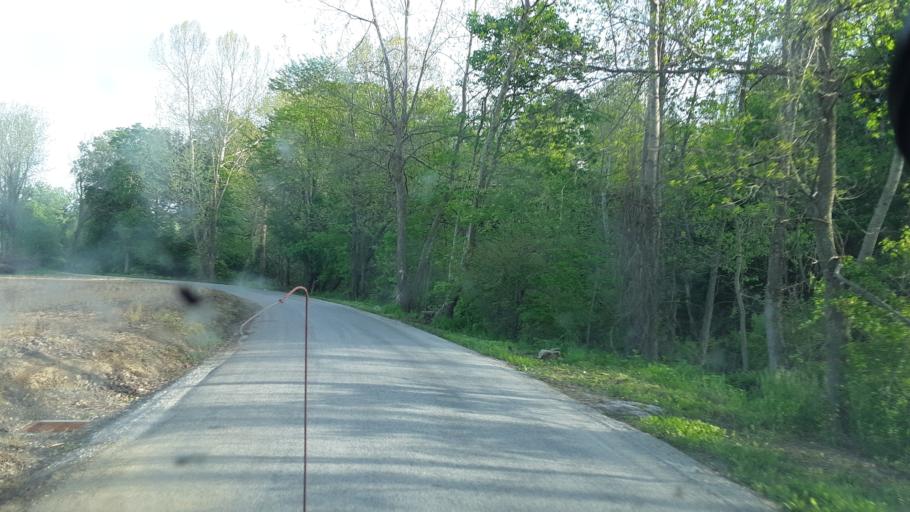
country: US
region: Ohio
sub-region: Ross County
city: Kingston
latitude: 39.4978
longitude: -82.7259
